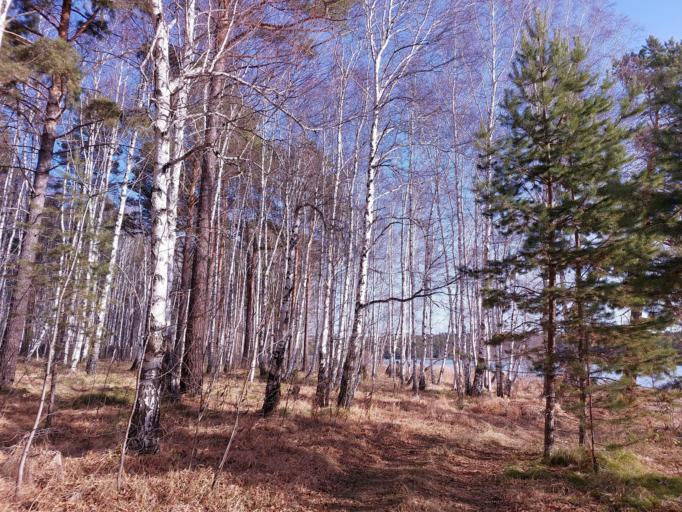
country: RU
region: Irkutsk
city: Pivovarikha
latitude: 52.1840
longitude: 104.4560
